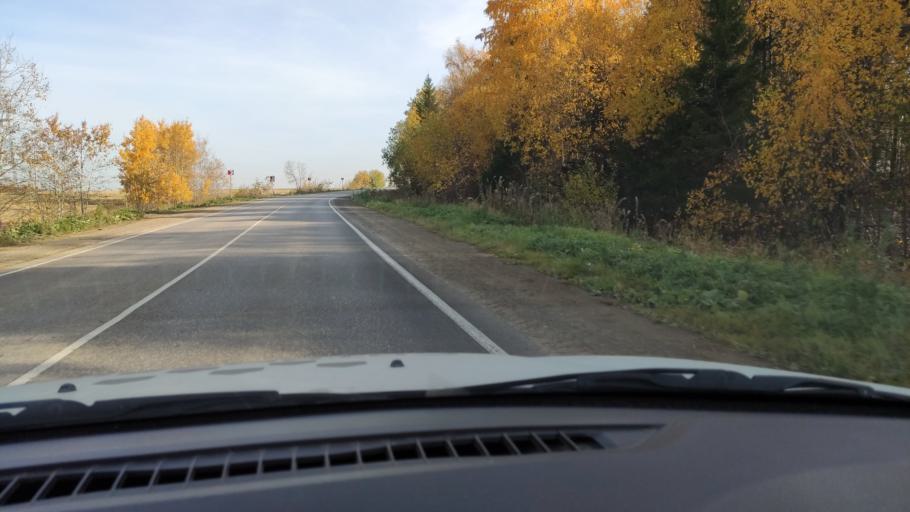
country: RU
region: Perm
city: Novyye Lyady
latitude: 58.0294
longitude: 56.6864
